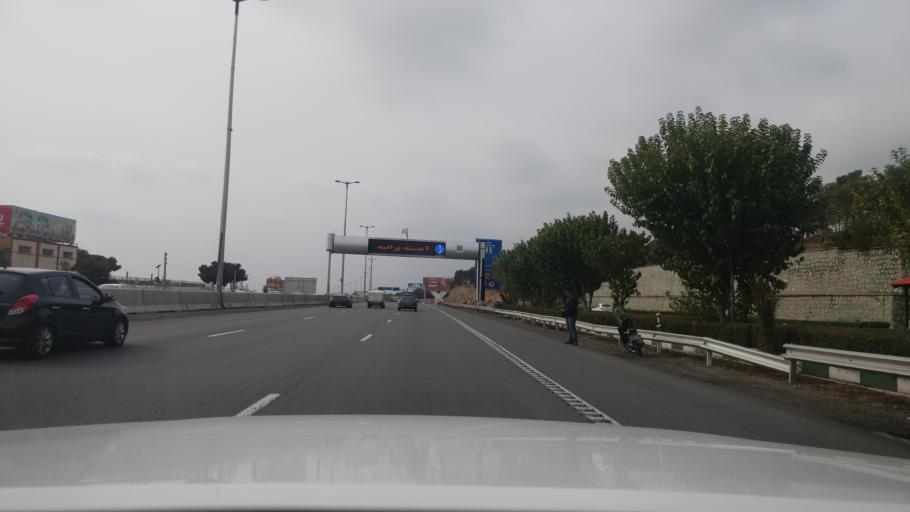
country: IR
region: Tehran
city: Shahr-e Qods
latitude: 35.7171
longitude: 51.2361
